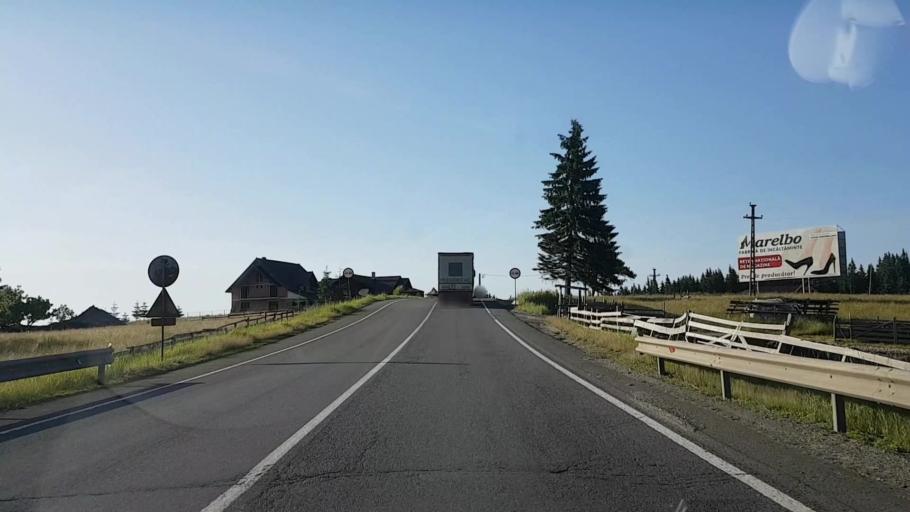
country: RO
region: Bistrita-Nasaud
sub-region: Comuna Lunca Ilvei
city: Lunca Ilvei
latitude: 47.2756
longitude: 25.0283
